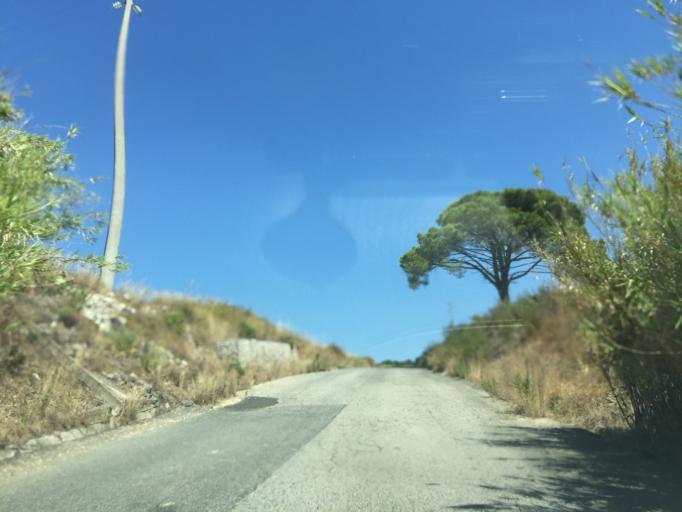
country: PT
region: Lisbon
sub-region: Alenquer
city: Carregado
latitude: 39.0459
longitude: -8.9287
